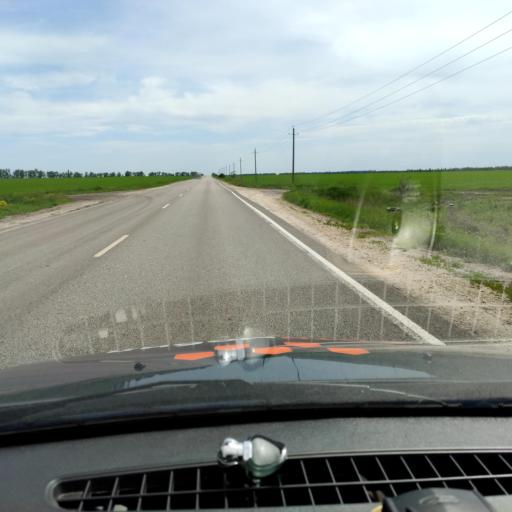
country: RU
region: Voronezj
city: Novaya Usman'
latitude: 51.5651
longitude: 39.3758
